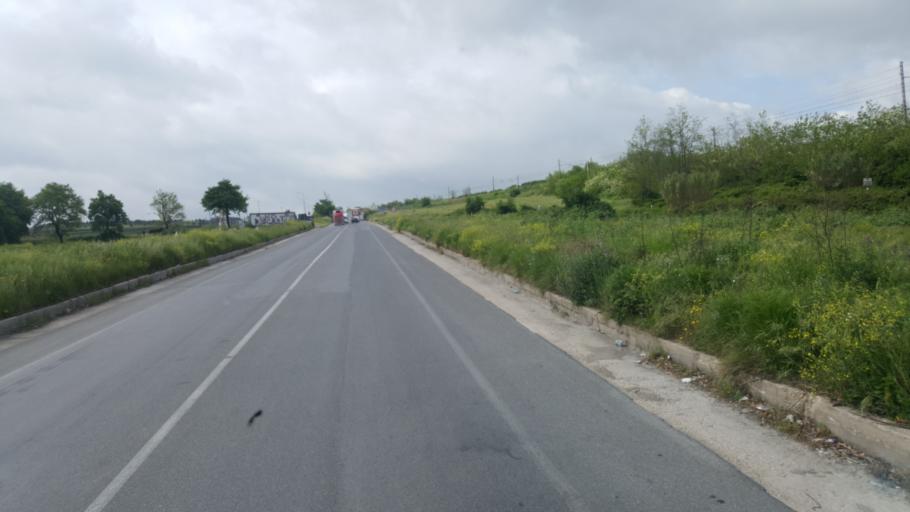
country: IT
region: Latium
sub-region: Citta metropolitana di Roma Capitale
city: Borgo Lotti
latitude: 41.7566
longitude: 12.5601
